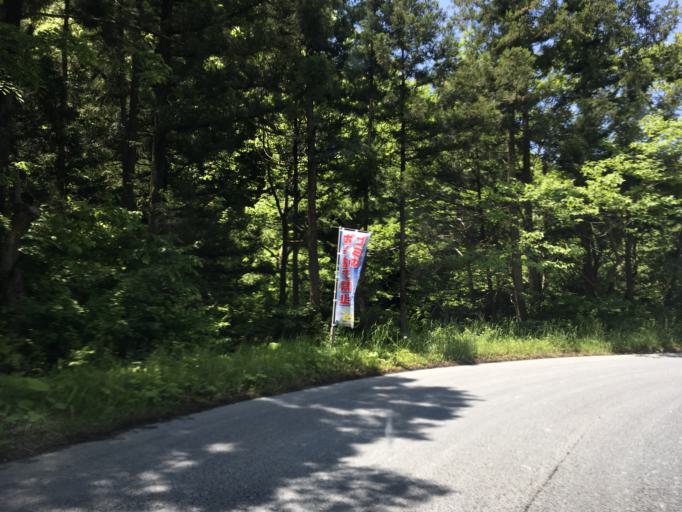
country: JP
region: Miyagi
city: Wakuya
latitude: 38.6564
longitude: 141.3191
